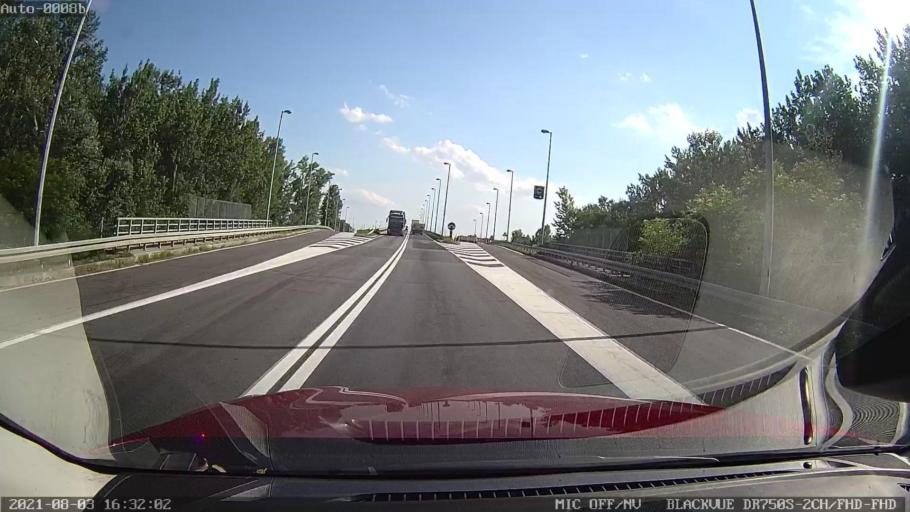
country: HR
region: Osjecko-Baranjska
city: Visnjevac
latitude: 45.5673
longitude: 18.6312
